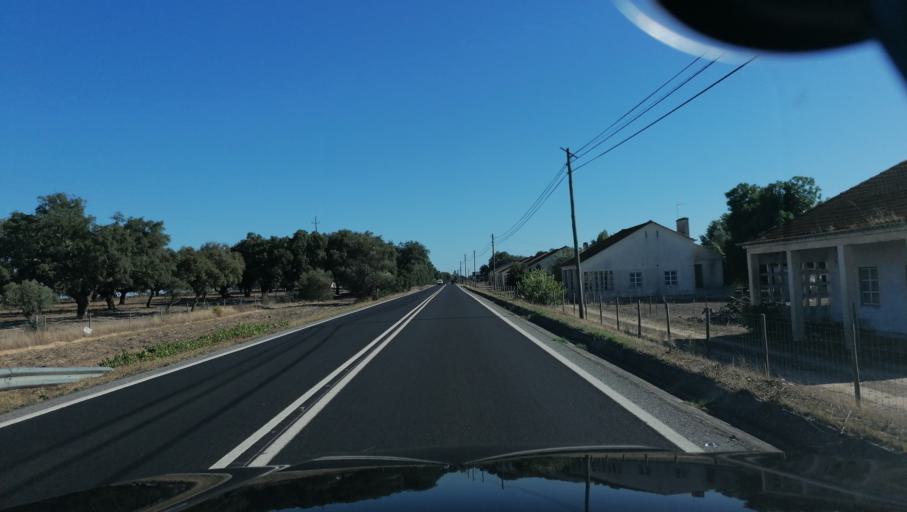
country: PT
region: Santarem
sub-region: Benavente
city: Poceirao
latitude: 38.8187
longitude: -8.8809
